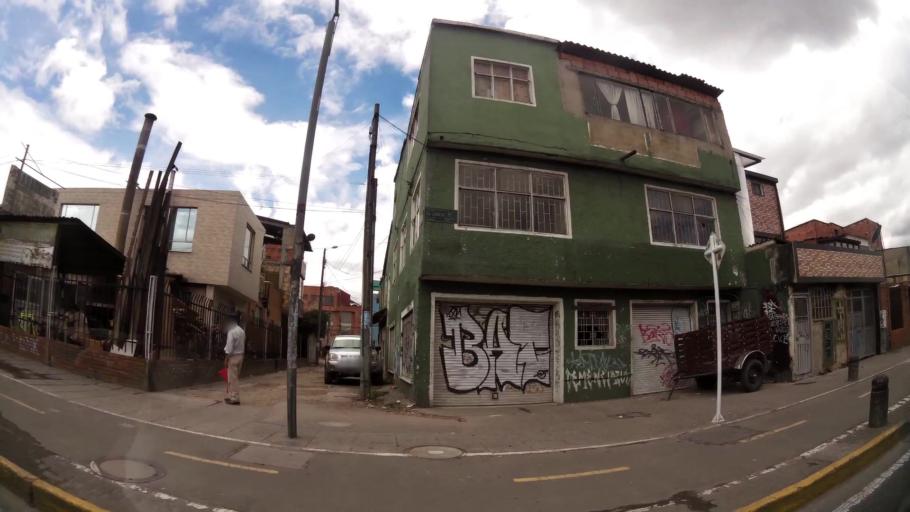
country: CO
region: Bogota D.C.
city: Bogota
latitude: 4.6924
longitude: -74.1077
